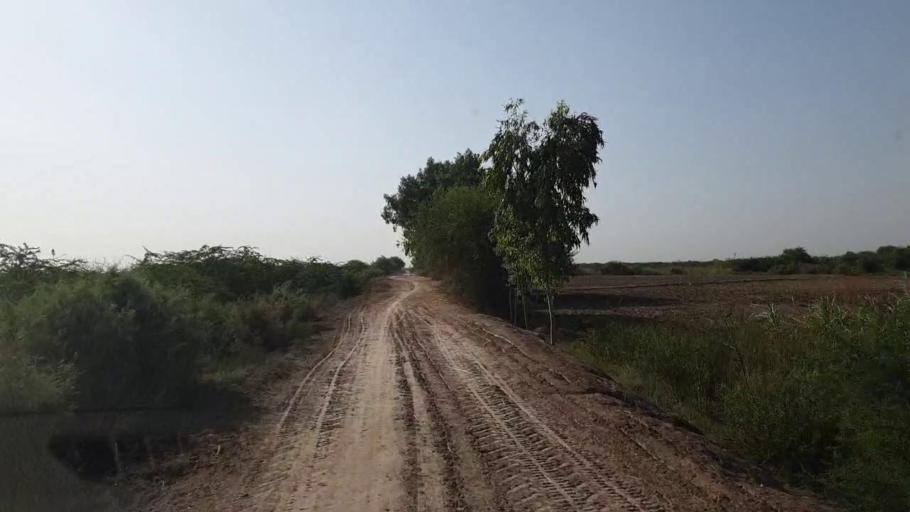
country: PK
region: Sindh
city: Kadhan
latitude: 24.6176
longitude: 69.0730
